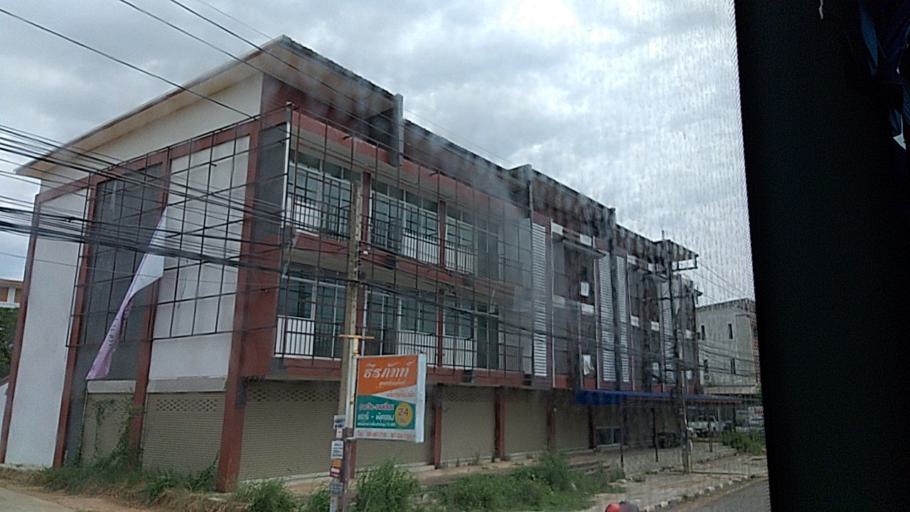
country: TH
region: Maha Sarakham
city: Maha Sarakham
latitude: 16.2246
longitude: 103.2719
